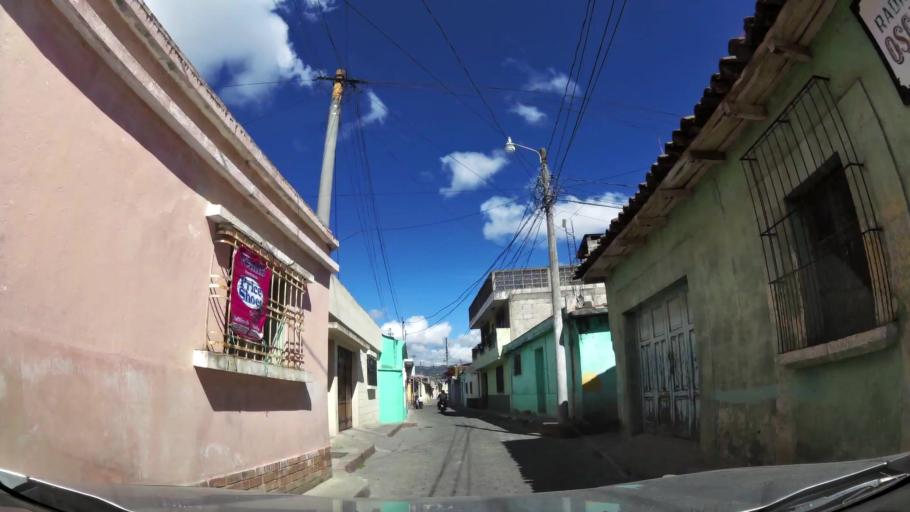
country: GT
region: Quetzaltenango
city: Quetzaltenango
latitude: 14.8375
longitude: -91.5156
